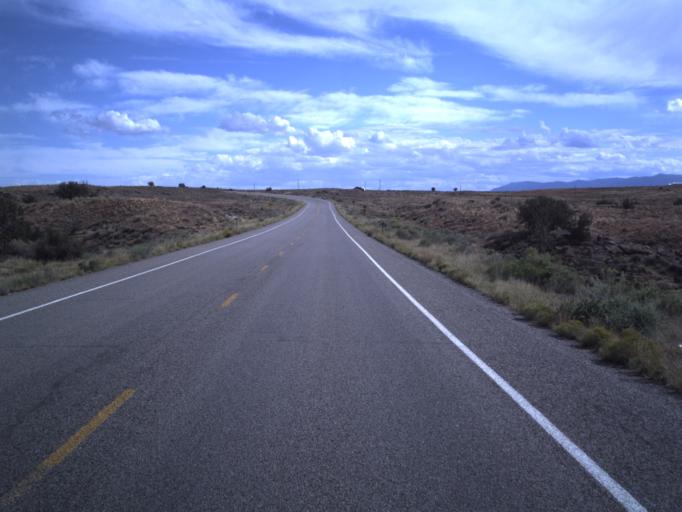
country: US
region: Colorado
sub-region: Montezuma County
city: Towaoc
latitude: 37.1840
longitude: -109.1263
